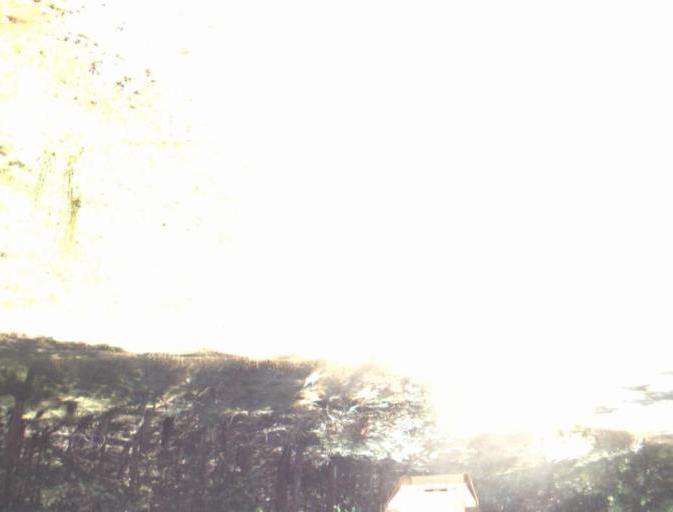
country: AU
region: Tasmania
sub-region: Dorset
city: Scottsdale
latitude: -41.2619
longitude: 147.3508
